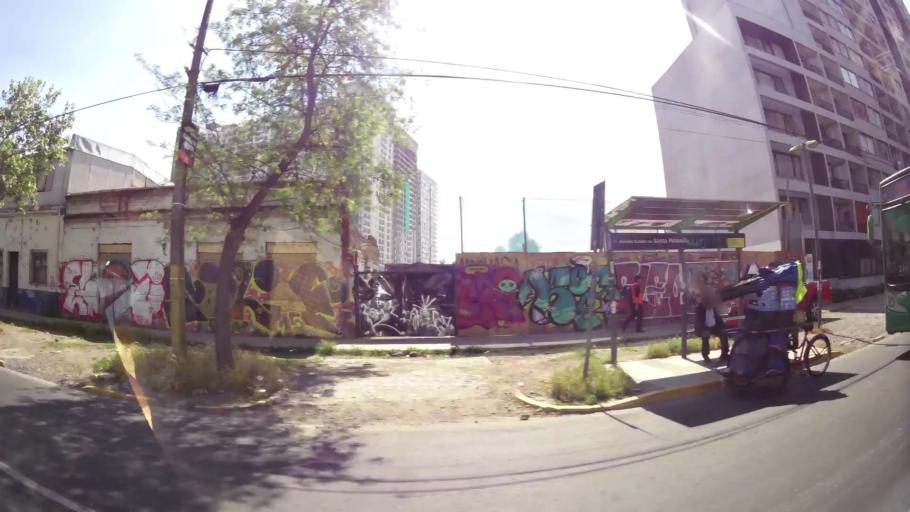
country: CL
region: Santiago Metropolitan
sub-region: Provincia de Santiago
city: Lo Prado
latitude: -33.4552
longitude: -70.7039
